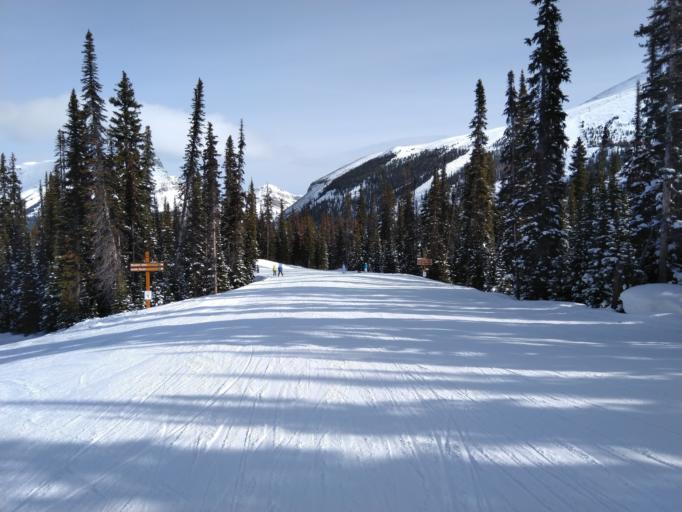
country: CA
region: Alberta
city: Banff
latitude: 51.0858
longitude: -115.7720
